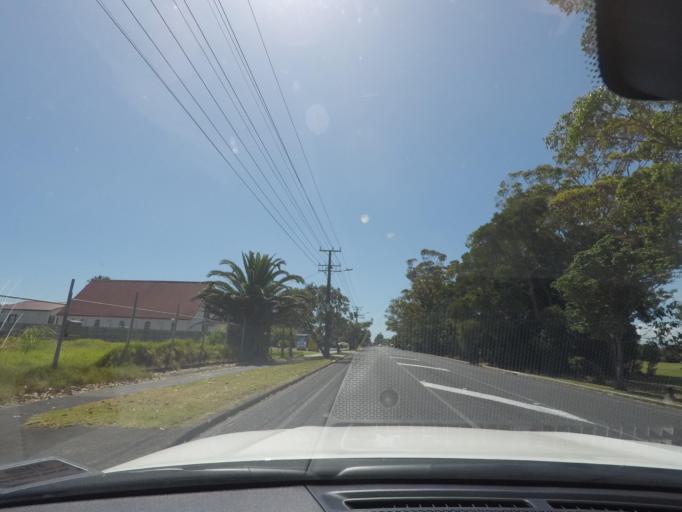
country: NZ
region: Auckland
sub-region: Auckland
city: Parakai
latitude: -36.6599
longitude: 174.4322
